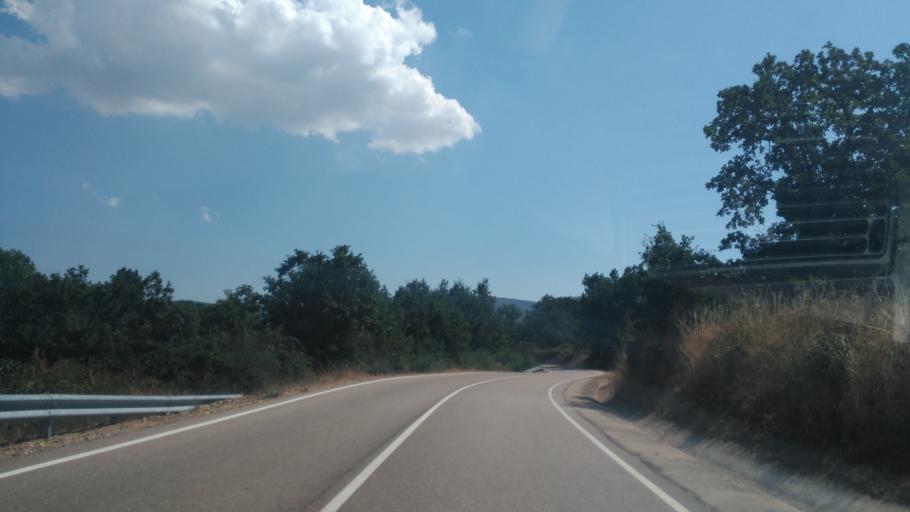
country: ES
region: Castille and Leon
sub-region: Provincia de Salamanca
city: Cereceda de la Sierra
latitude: 40.5664
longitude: -6.0996
